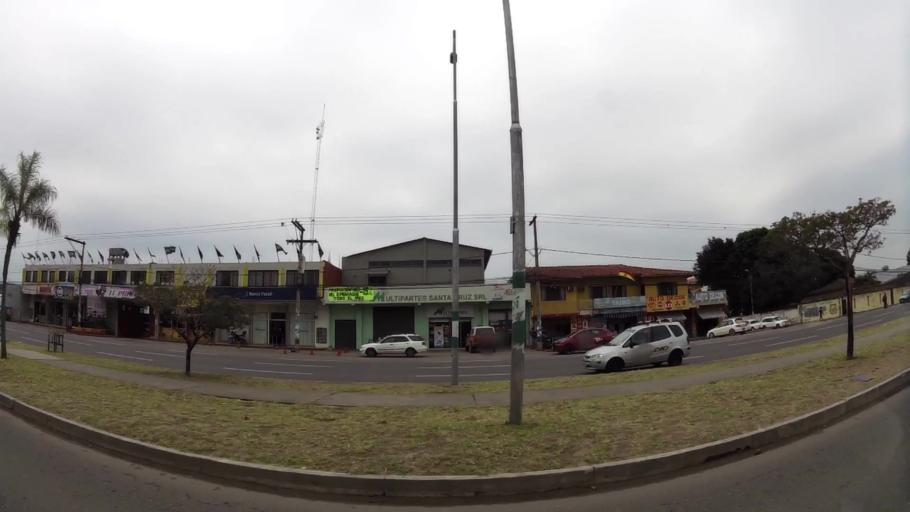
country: BO
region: Santa Cruz
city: Santa Cruz de la Sierra
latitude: -17.7999
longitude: -63.1945
